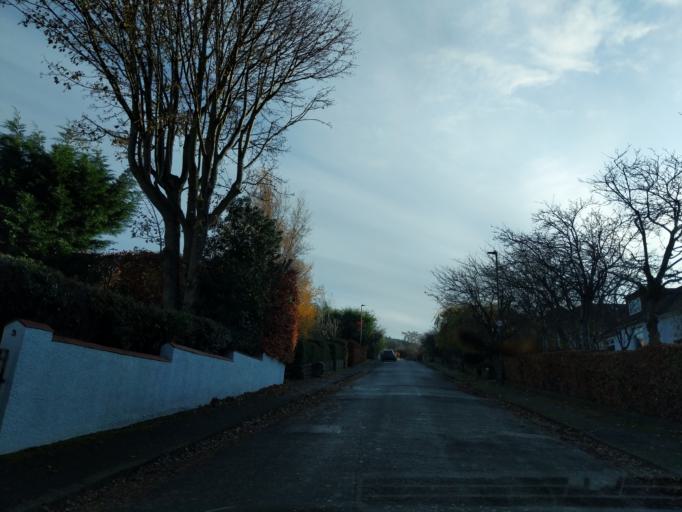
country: GB
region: Scotland
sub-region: Edinburgh
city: Colinton
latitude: 55.9029
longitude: -3.2661
